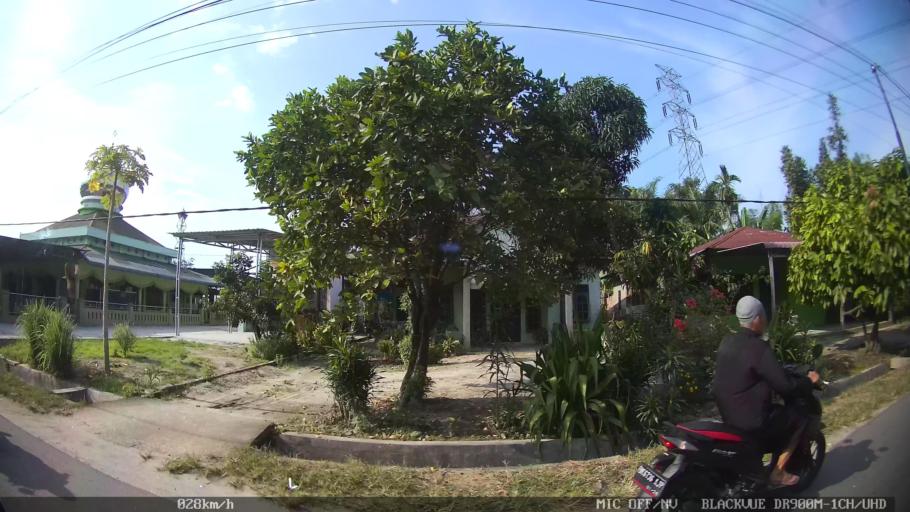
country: ID
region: North Sumatra
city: Percut
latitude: 3.5939
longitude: 98.7882
